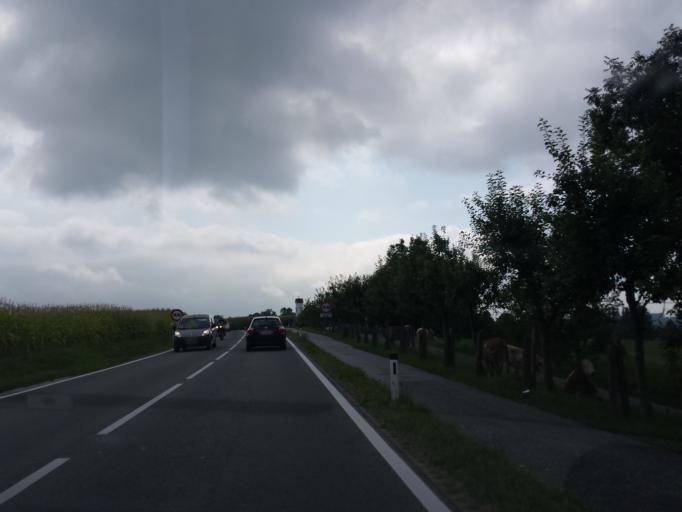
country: AT
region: Styria
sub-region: Politischer Bezirk Deutschlandsberg
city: Rassach
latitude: 46.8639
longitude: 15.2648
